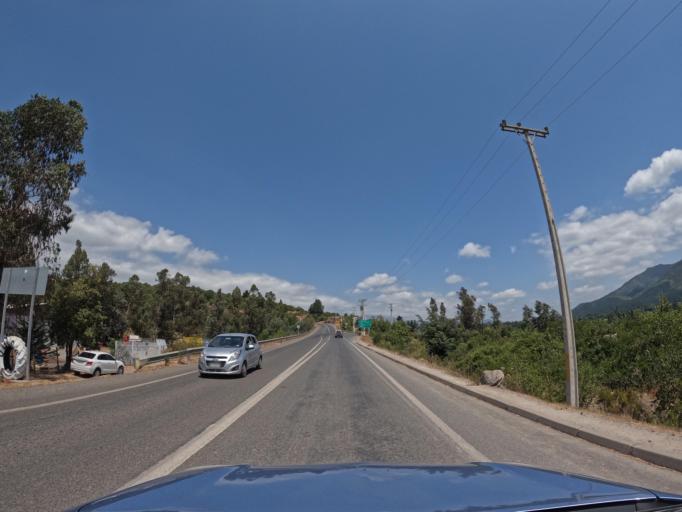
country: CL
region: Maule
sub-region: Provincia de Curico
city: Molina
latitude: -35.1794
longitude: -71.1194
